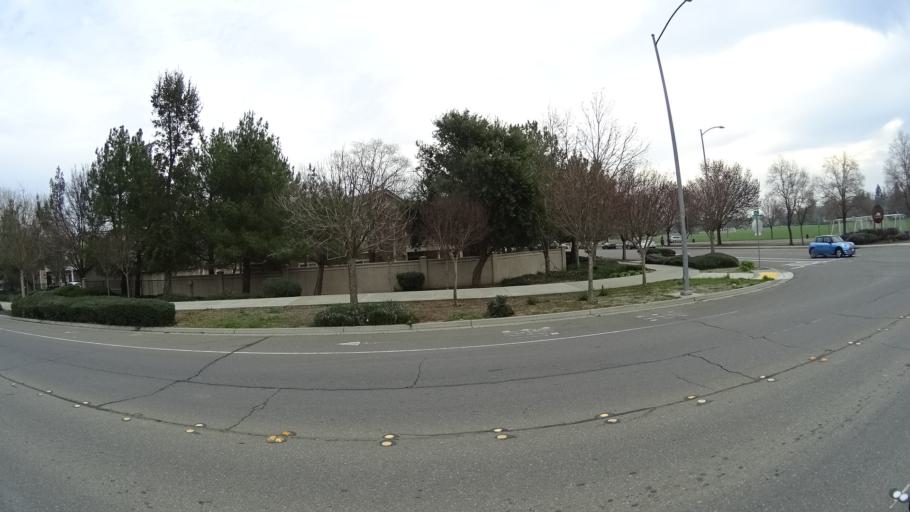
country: US
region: California
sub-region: Yolo County
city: Davis
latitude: 38.5706
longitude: -121.7307
